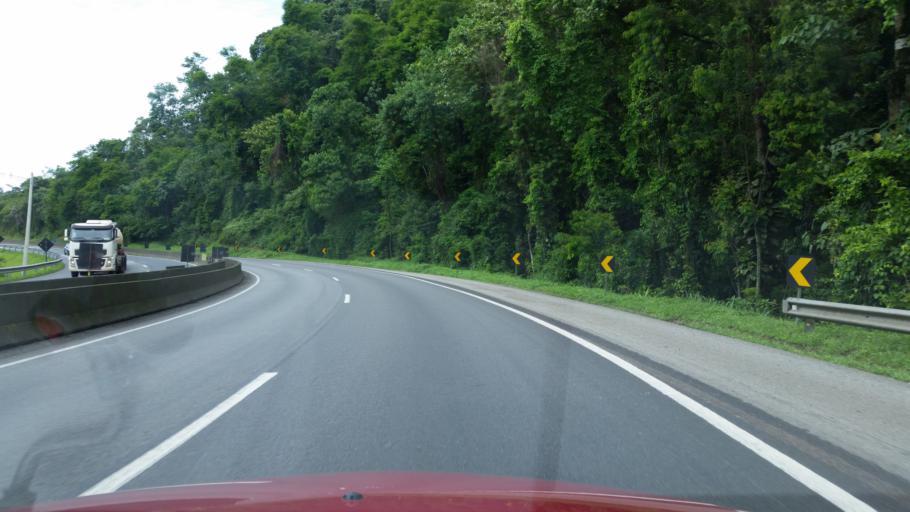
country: BR
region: Sao Paulo
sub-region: Miracatu
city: Miracatu
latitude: -24.1382
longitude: -47.2734
